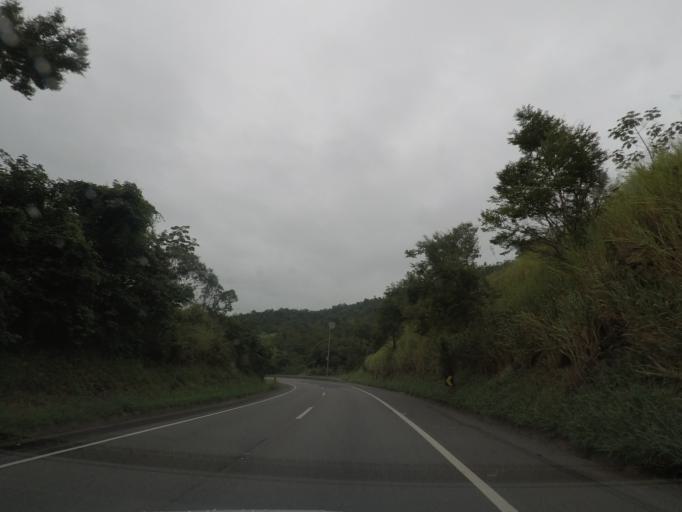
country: BR
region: Sao Paulo
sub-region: Cajati
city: Cajati
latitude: -24.7904
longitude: -48.2055
